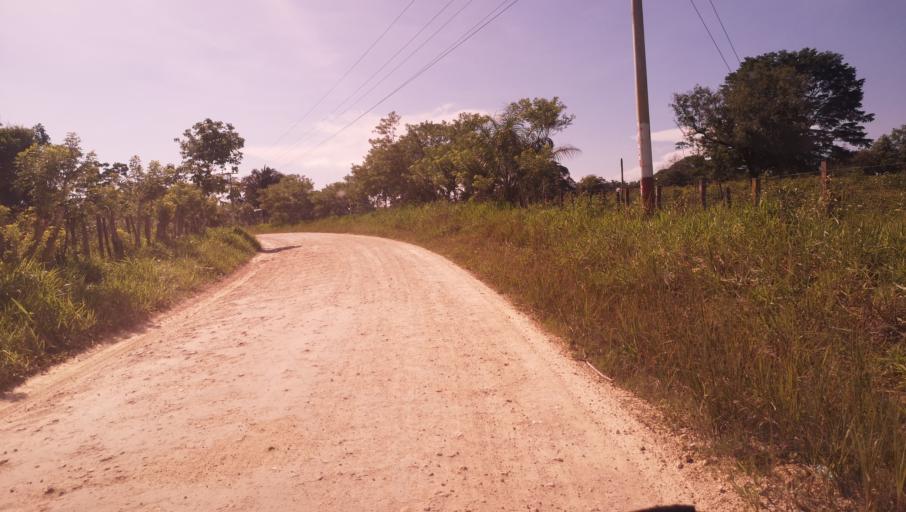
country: GT
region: Peten
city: Dolores
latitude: 16.7148
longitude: -89.3669
